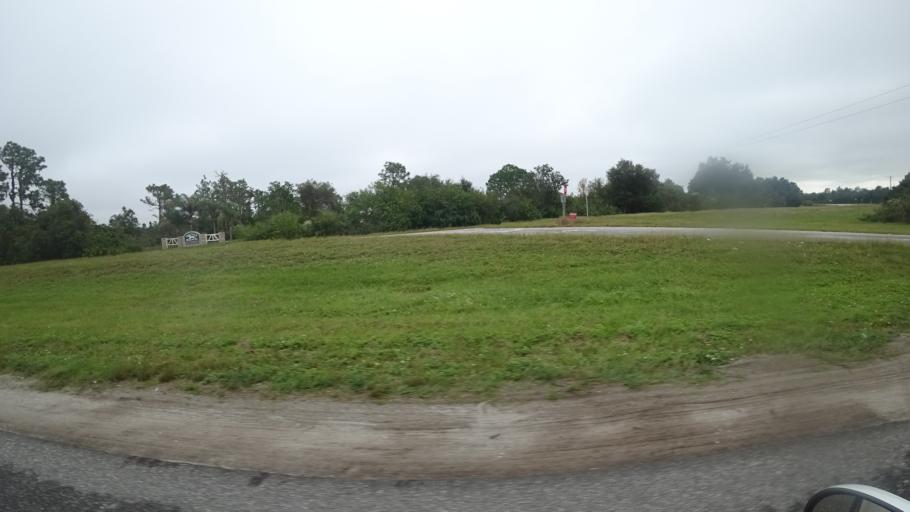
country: US
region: Florida
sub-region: Sarasota County
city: Fruitville
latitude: 27.4004
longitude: -82.3040
